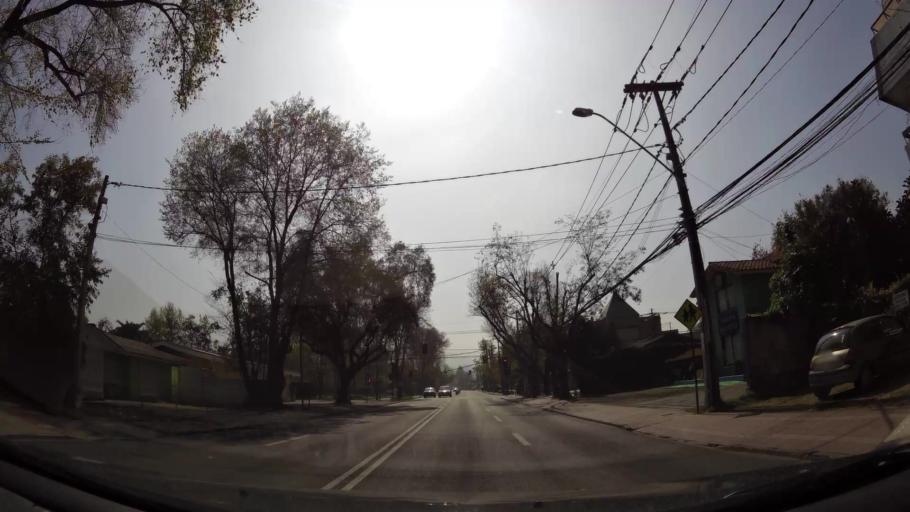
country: CL
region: Santiago Metropolitan
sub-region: Provincia de Santiago
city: Villa Presidente Frei, Nunoa, Santiago, Chile
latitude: -33.3847
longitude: -70.5743
